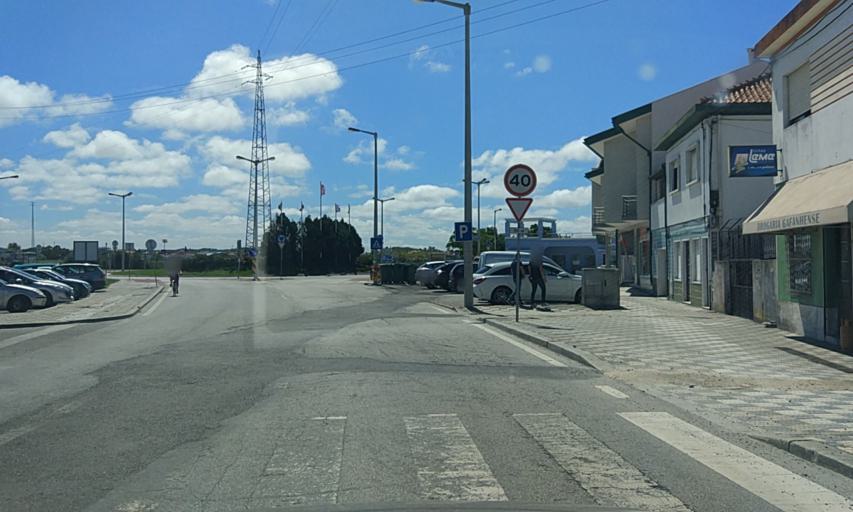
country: PT
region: Aveiro
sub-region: Ilhavo
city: Ilhavo
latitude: 40.6089
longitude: -8.6846
